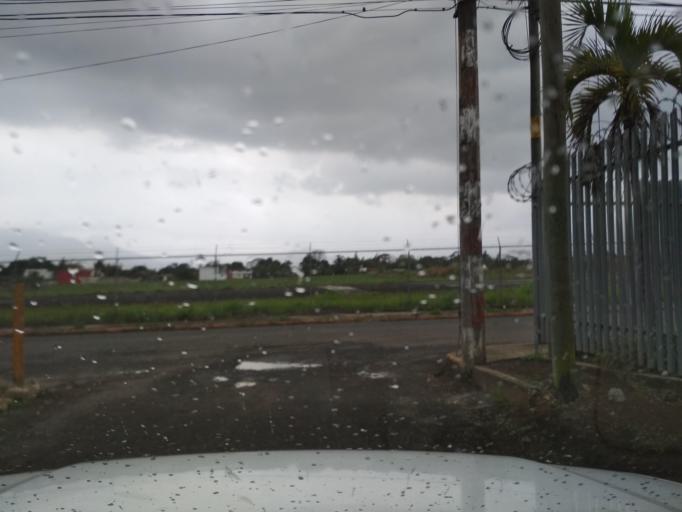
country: MX
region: Veracruz
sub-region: Cordoba
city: Veinte de Noviembre
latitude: 18.8712
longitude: -96.9535
